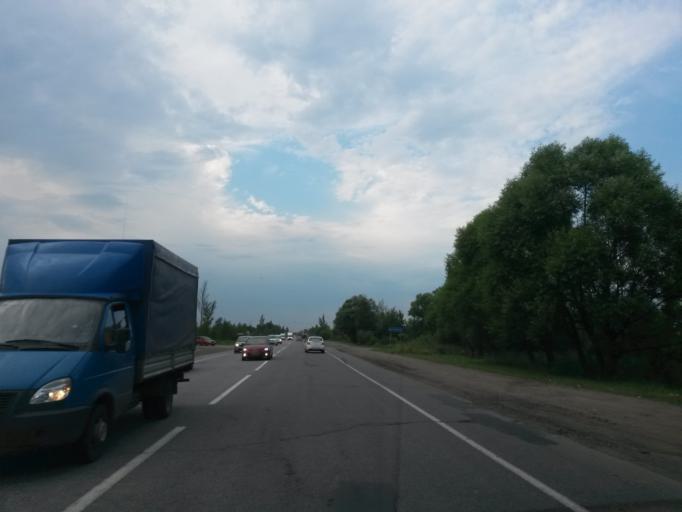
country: RU
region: Jaroslavl
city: Yaroslavl
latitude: 57.6064
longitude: 39.7920
